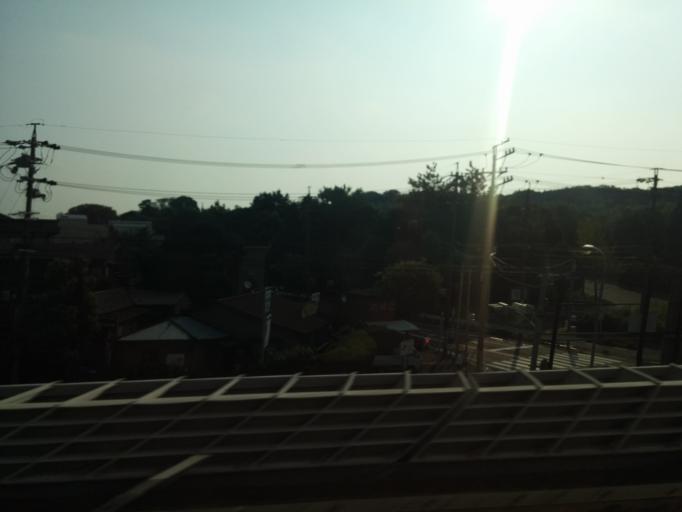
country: JP
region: Aichi
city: Obu
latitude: 35.0628
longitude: 136.9442
